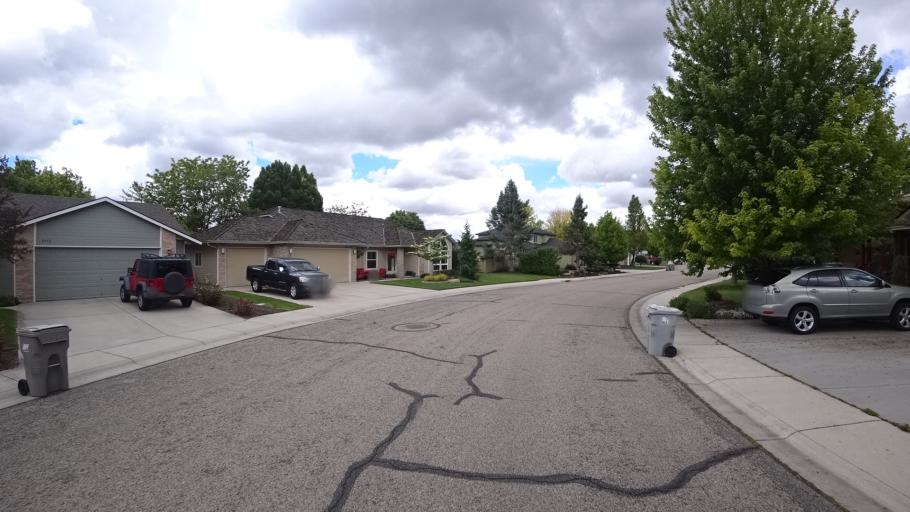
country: US
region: Idaho
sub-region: Ada County
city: Garden City
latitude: 43.6698
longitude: -116.2624
